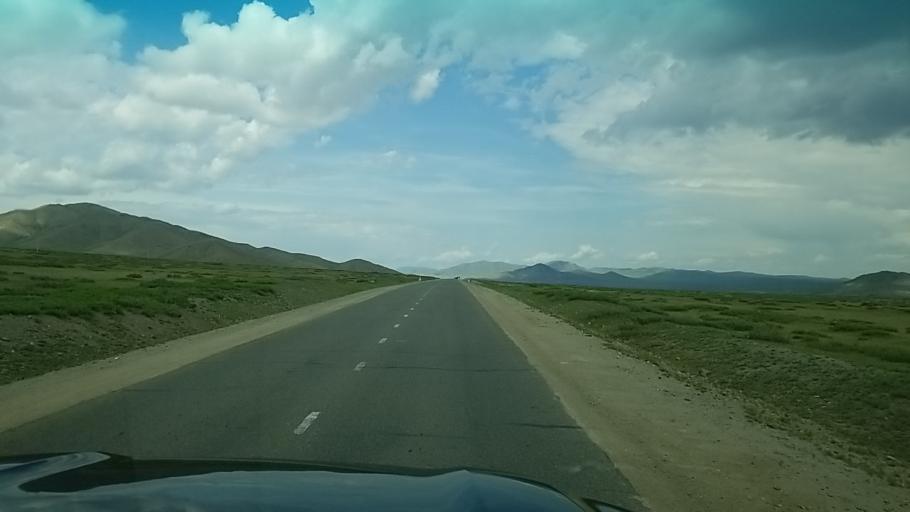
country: MN
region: Darhan Uul
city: Orhon
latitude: 49.7190
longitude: 106.1084
